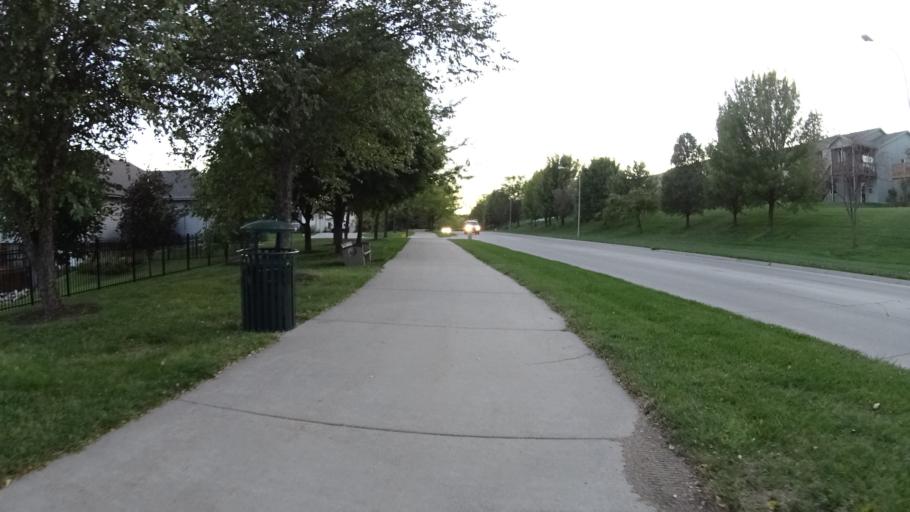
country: US
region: Nebraska
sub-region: Sarpy County
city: Papillion
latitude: 41.1358
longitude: -95.9880
